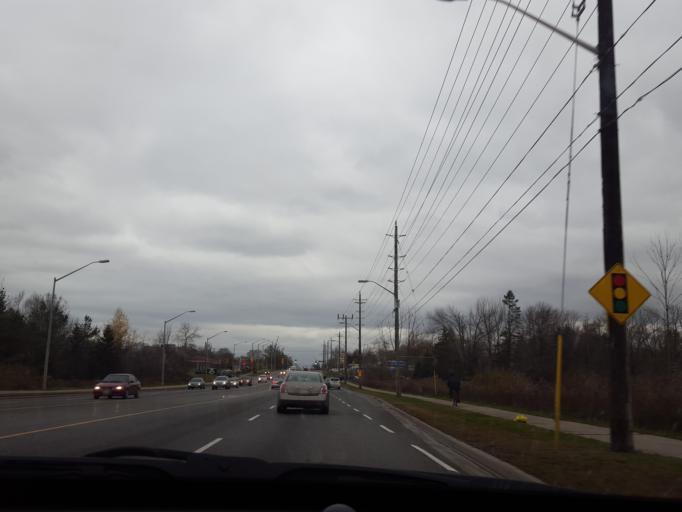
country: CA
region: Ontario
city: Ajax
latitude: 43.8474
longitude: -79.0032
